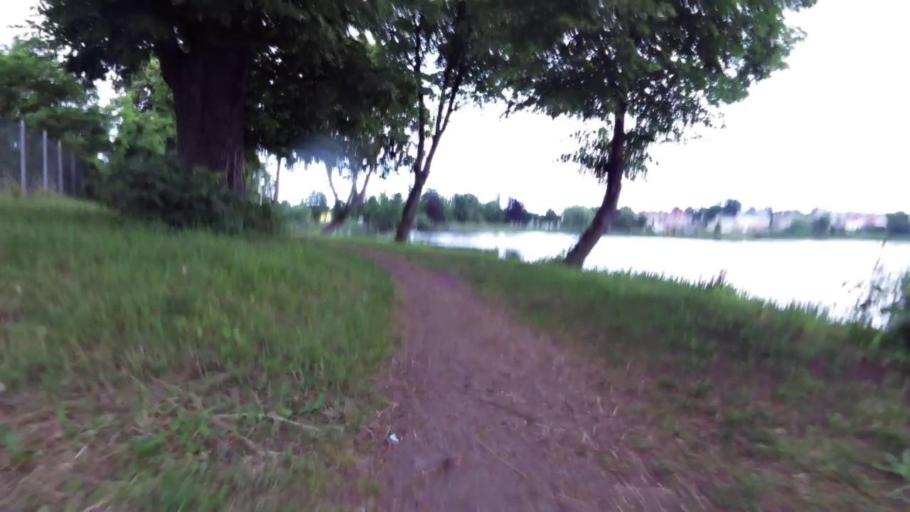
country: PL
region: West Pomeranian Voivodeship
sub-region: Powiat stargardzki
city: Chociwel
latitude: 53.4637
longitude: 15.3353
